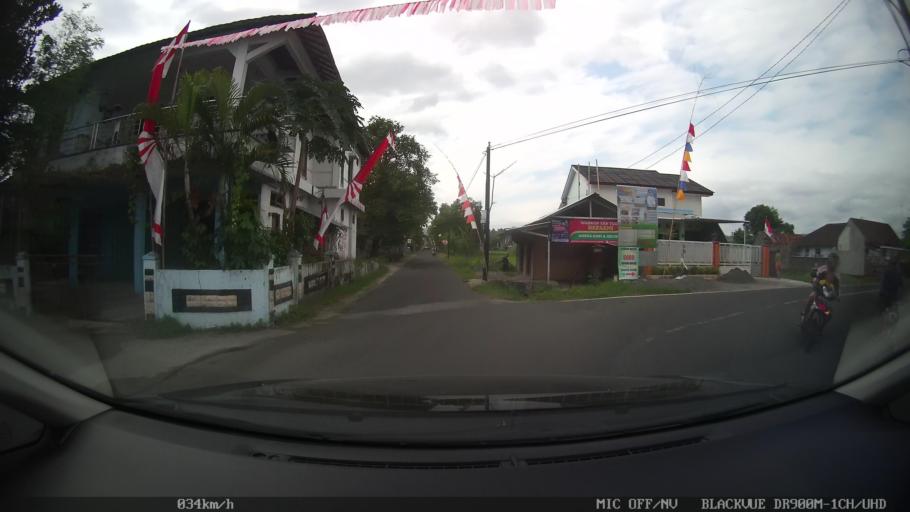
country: ID
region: Daerah Istimewa Yogyakarta
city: Depok
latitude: -7.8067
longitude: 110.4619
